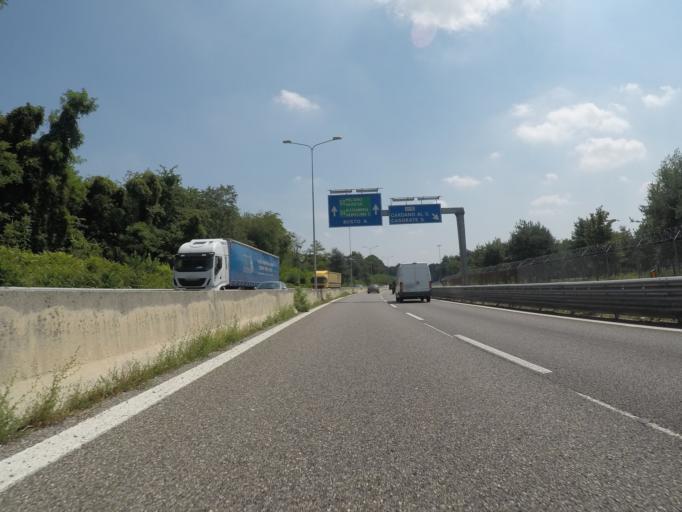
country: IT
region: Lombardy
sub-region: Provincia di Varese
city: Casorate Sempione
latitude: 45.6549
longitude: 8.7383
